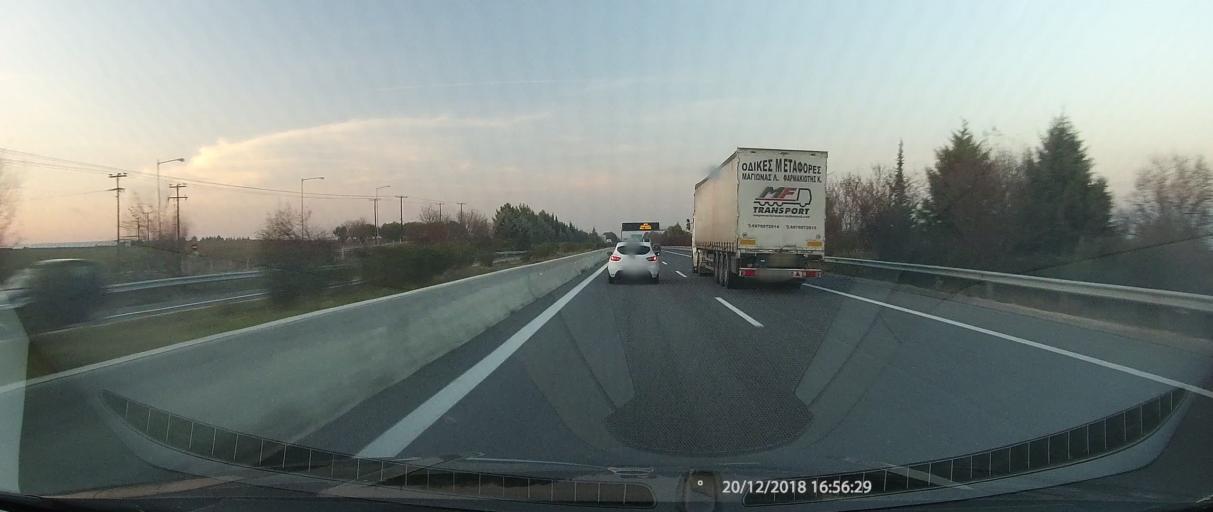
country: GR
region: Thessaly
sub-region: Nomos Larisis
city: Nikaia
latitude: 39.5558
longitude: 22.4916
